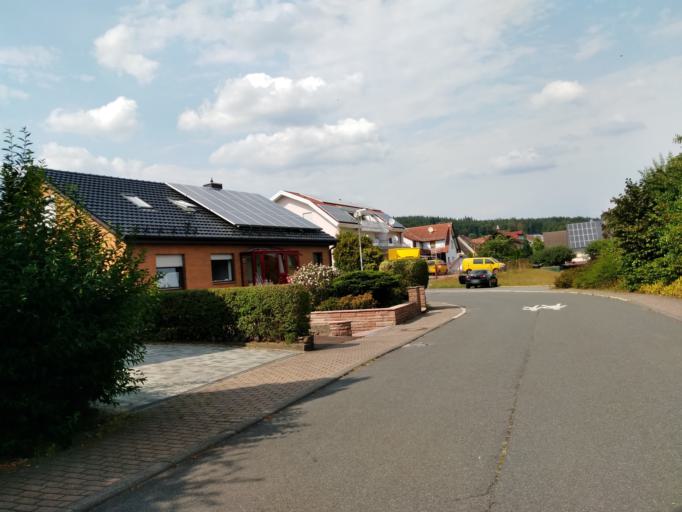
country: DE
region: Baden-Wuerttemberg
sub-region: Karlsruhe Region
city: Limbach
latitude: 49.4580
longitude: 9.2073
